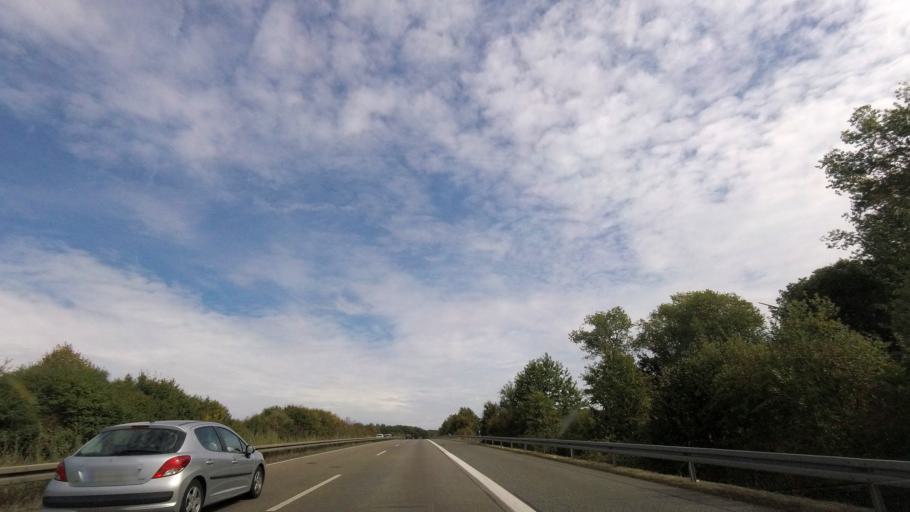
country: DE
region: Hesse
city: Kirtorf
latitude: 50.7105
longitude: 9.0667
